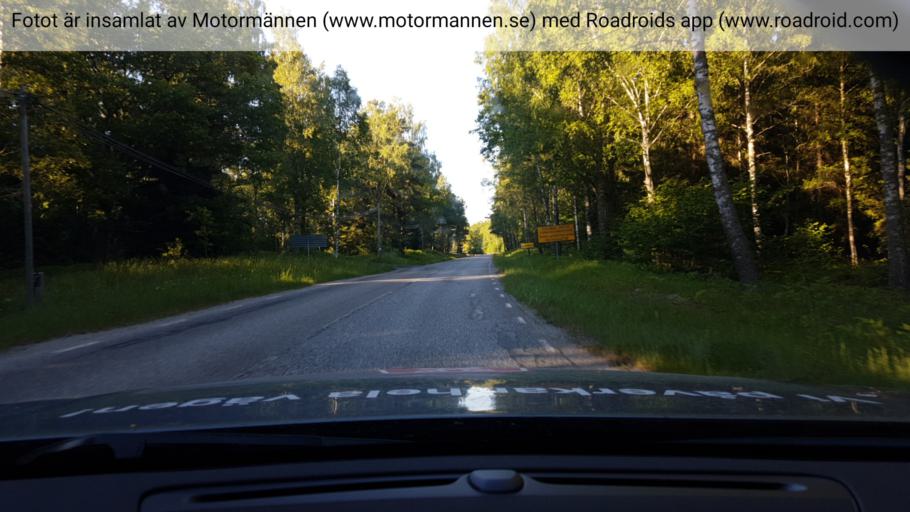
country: SE
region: Stockholm
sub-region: Haninge Kommun
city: Jordbro
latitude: 58.9940
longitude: 18.1013
